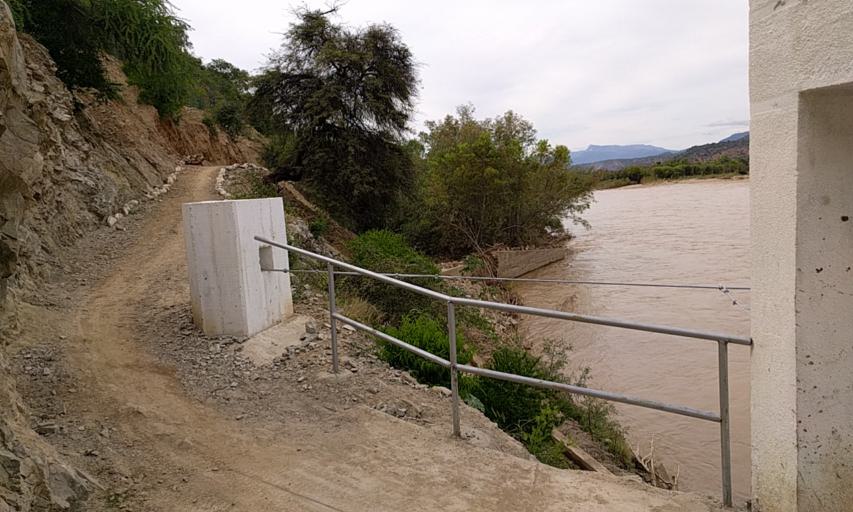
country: BO
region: Cochabamba
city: Aiquile
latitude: -18.0810
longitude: -64.9281
